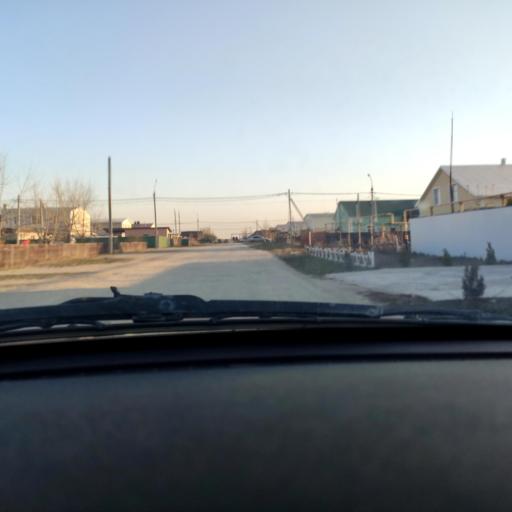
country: RU
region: Samara
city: Podstepki
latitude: 53.5719
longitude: 49.1190
